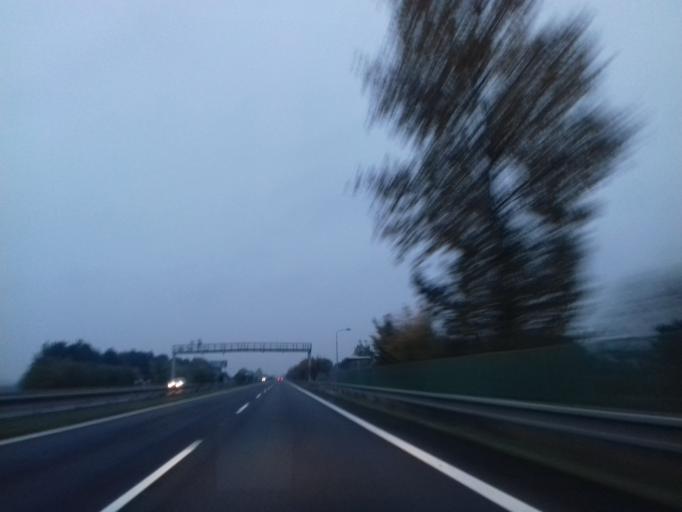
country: CZ
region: Olomoucky
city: Naklo
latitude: 49.6499
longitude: 17.1253
